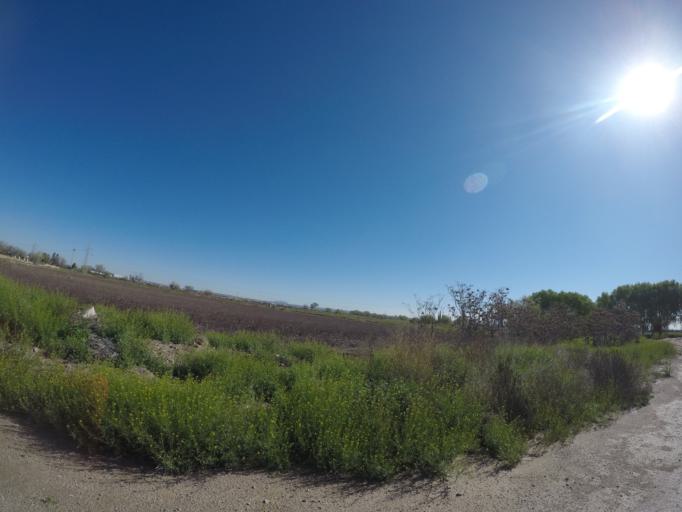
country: US
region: Texas
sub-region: El Paso County
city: Socorro
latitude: 31.6467
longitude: -106.3400
